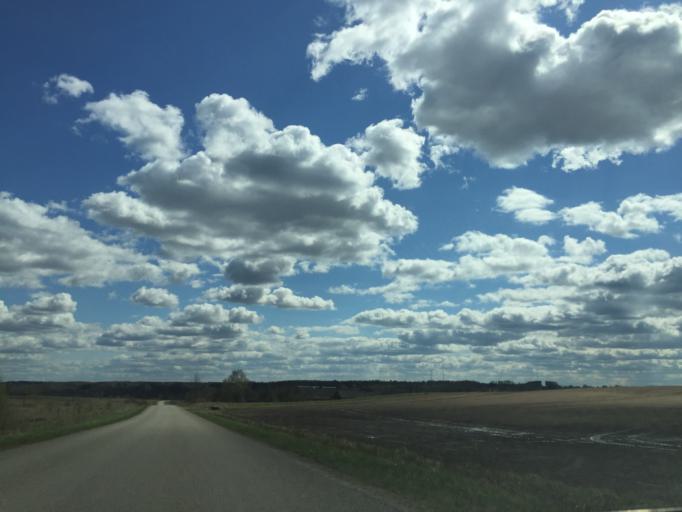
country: LV
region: Rezekne
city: Rezekne
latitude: 56.5570
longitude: 27.1469
